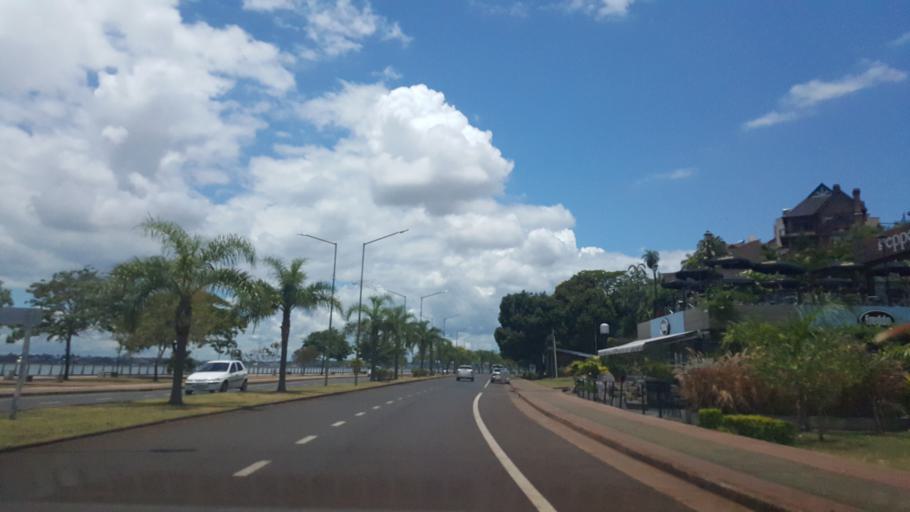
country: AR
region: Misiones
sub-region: Departamento de Capital
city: Posadas
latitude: -27.3520
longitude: -55.8974
